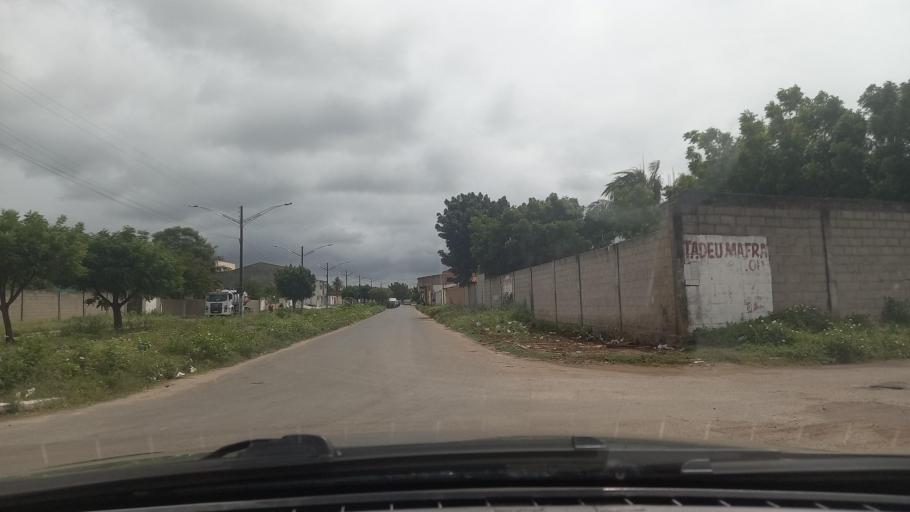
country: BR
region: Alagoas
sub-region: Delmiro Gouveia
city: Delmiro Gouveia
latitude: -9.3864
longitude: -38.0015
